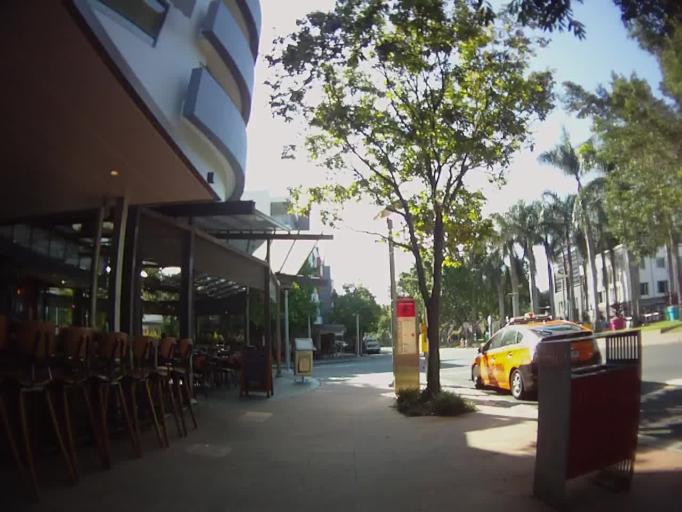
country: AU
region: Queensland
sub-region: Brisbane
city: South Brisbane
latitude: -27.4791
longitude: 153.0225
